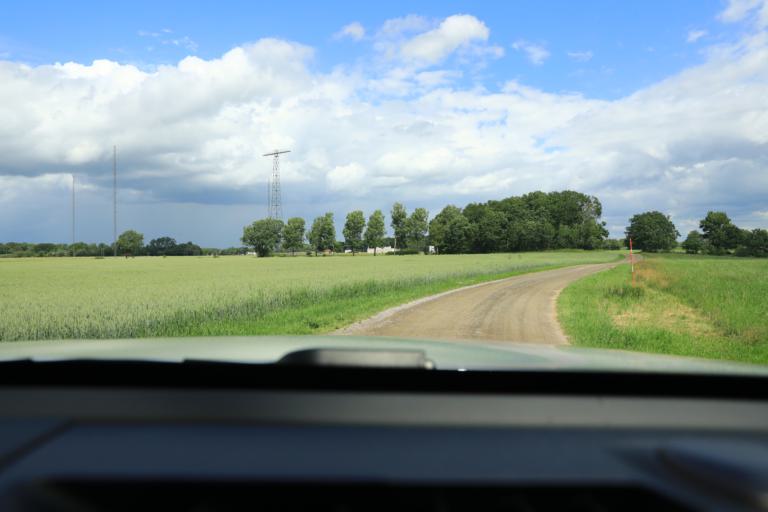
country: SE
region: Halland
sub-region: Varbergs Kommun
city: Tvaaker
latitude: 57.1074
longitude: 12.4030
